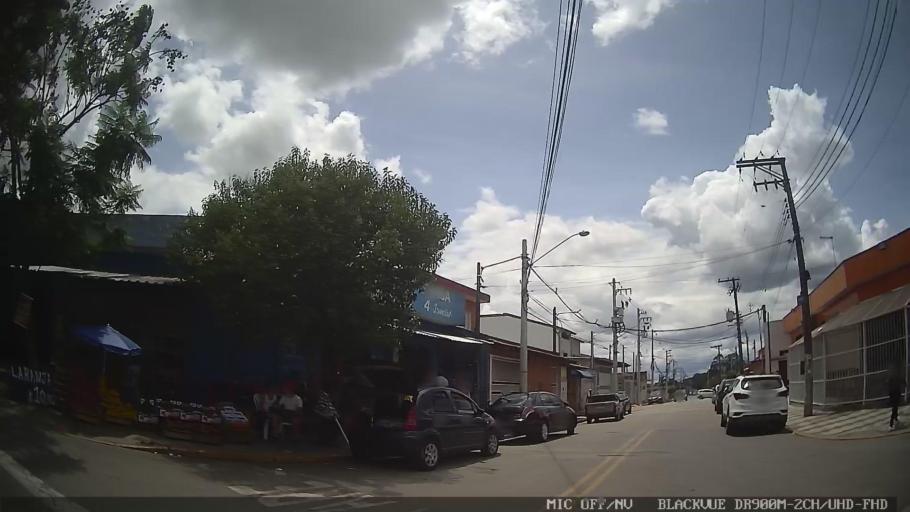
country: BR
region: Sao Paulo
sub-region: Mogi das Cruzes
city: Mogi das Cruzes
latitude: -23.5728
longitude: -46.2172
